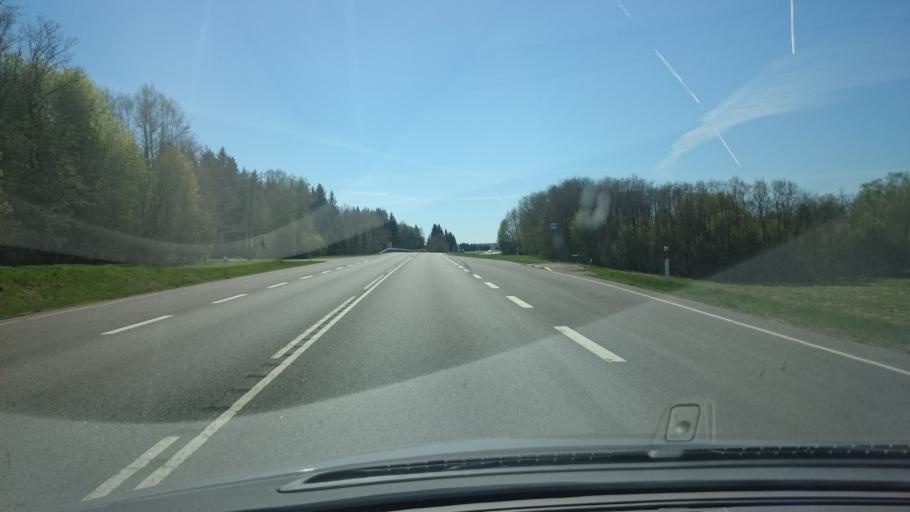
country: EE
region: Ida-Virumaa
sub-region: Narva-Joesuu linn
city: Narva-Joesuu
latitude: 59.3792
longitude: 27.9586
